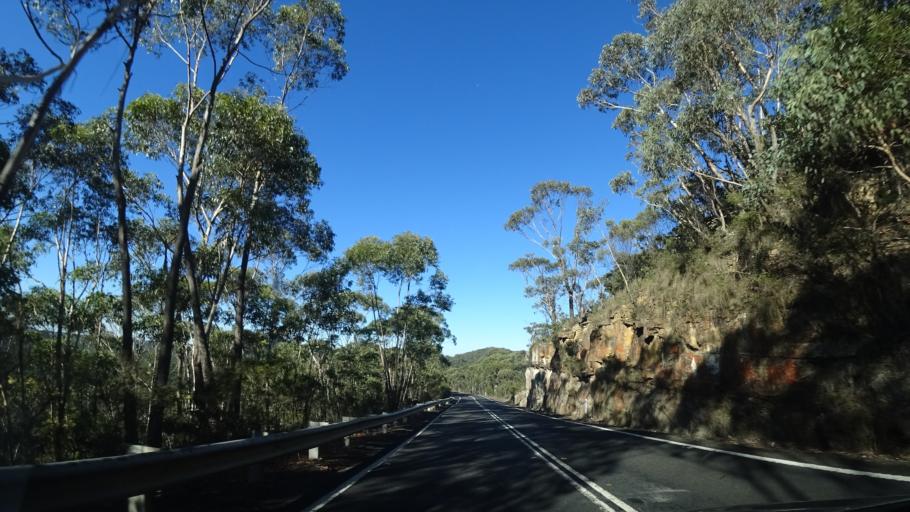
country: AU
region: New South Wales
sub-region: Blue Mountains Municipality
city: Blackheath
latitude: -33.5554
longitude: 150.3757
